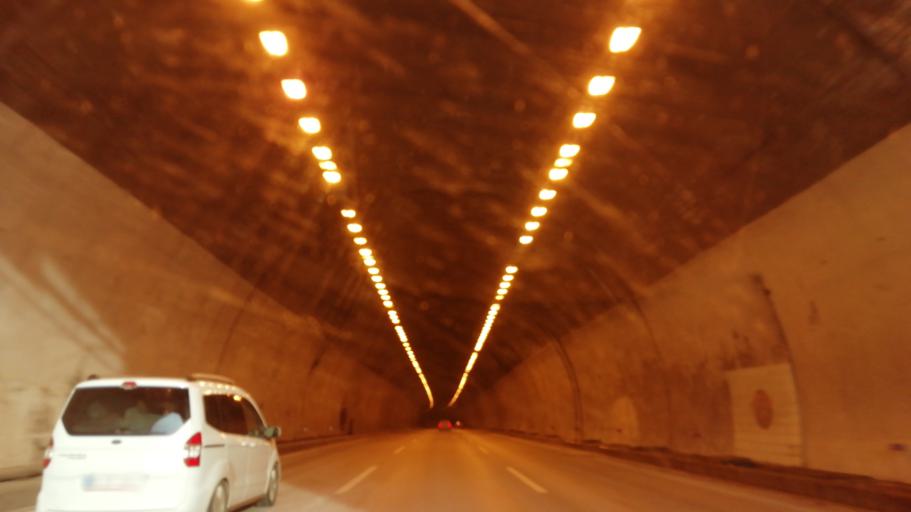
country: TR
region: Duzce
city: Kaynasli
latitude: 40.7361
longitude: 31.4495
